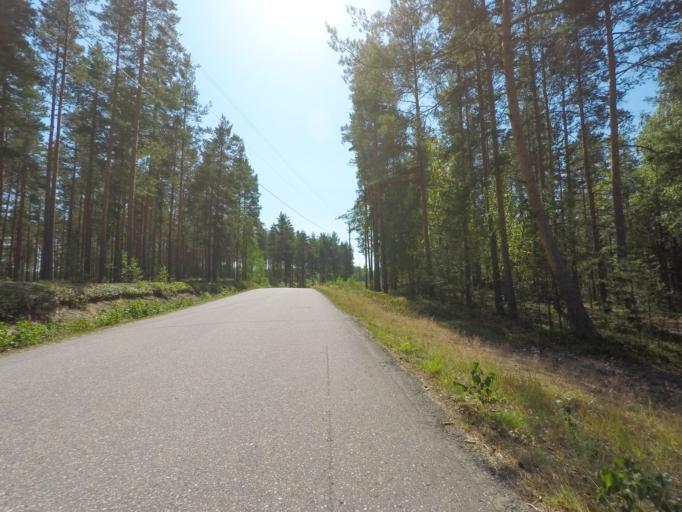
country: FI
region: Southern Savonia
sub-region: Mikkeli
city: Puumala
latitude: 61.4324
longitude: 28.1701
